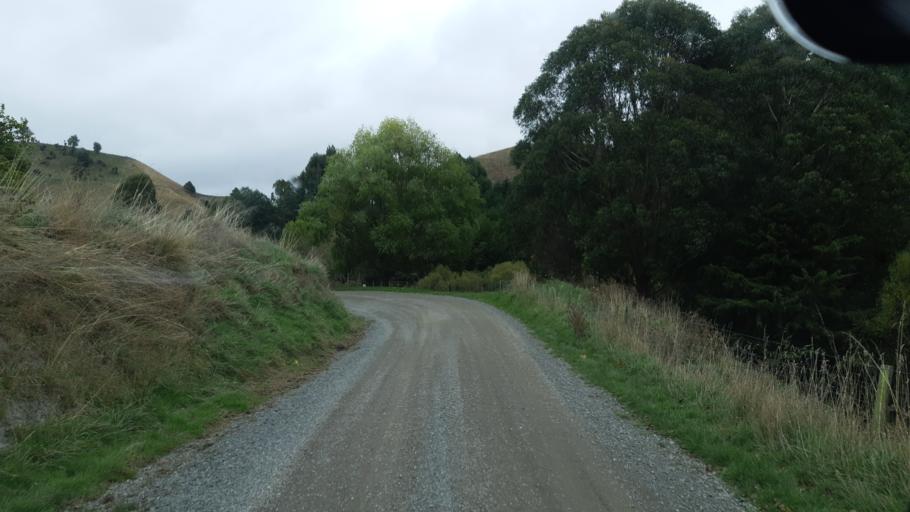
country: NZ
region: Manawatu-Wanganui
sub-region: Ruapehu District
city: Waiouru
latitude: -39.6048
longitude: 175.5776
